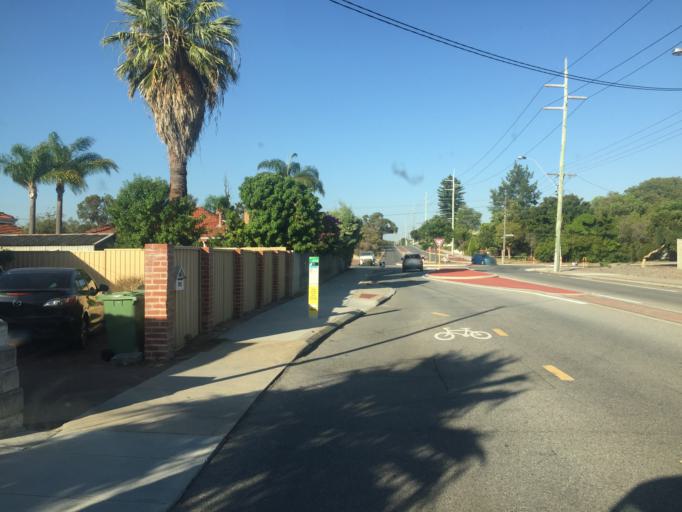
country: AU
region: Western Australia
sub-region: Belmont
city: Belmont
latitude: -31.9552
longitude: 115.9351
